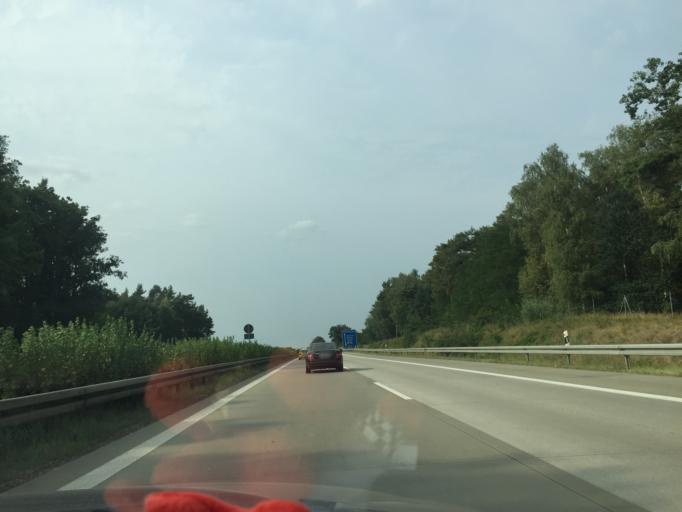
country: DE
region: Brandenburg
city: Mittenwalde
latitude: 52.2403
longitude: 13.5916
